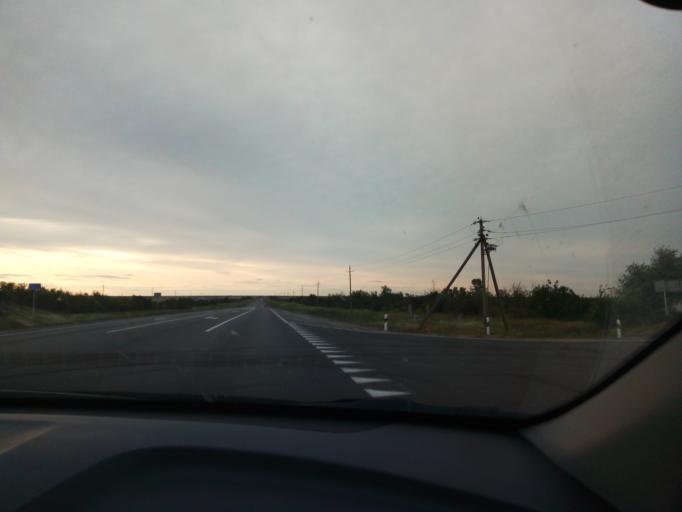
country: RU
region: Volgograd
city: Primorsk
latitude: 49.2368
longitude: 44.8973
